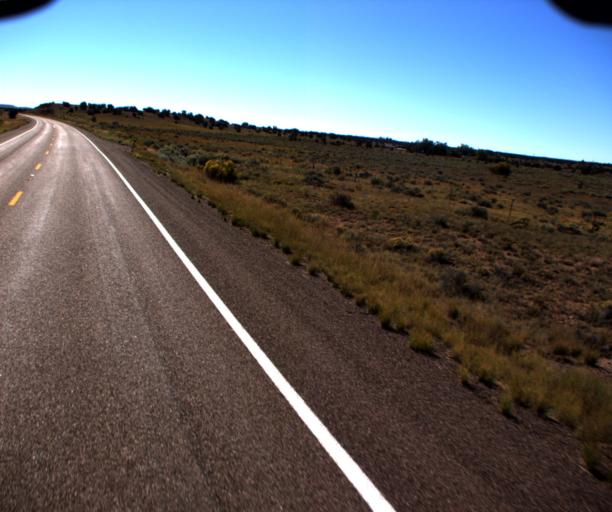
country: US
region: Arizona
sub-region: Apache County
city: Saint Johns
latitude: 34.6085
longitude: -109.6482
